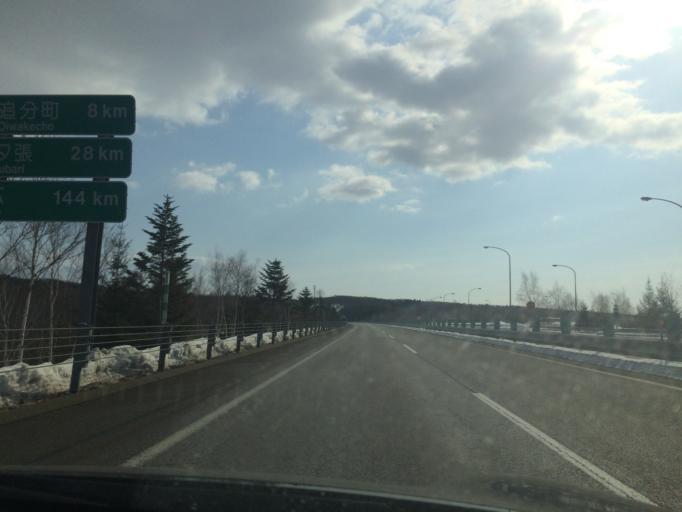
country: JP
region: Hokkaido
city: Chitose
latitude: 42.8787
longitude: 141.7259
